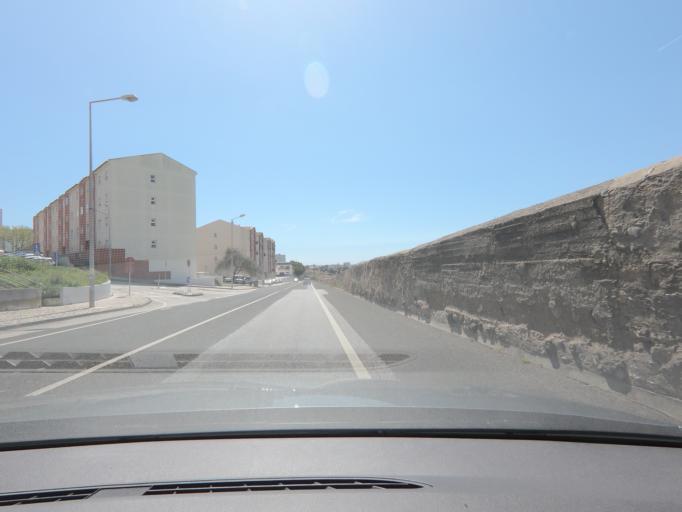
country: PT
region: Lisbon
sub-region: Oeiras
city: Oeiras
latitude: 38.7001
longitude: -9.3097
